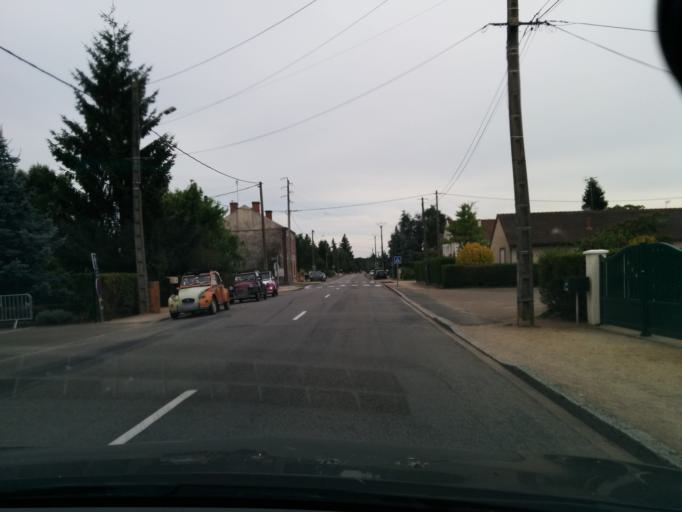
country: FR
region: Centre
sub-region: Departement du Loiret
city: Tigy
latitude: 47.7937
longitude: 2.1982
